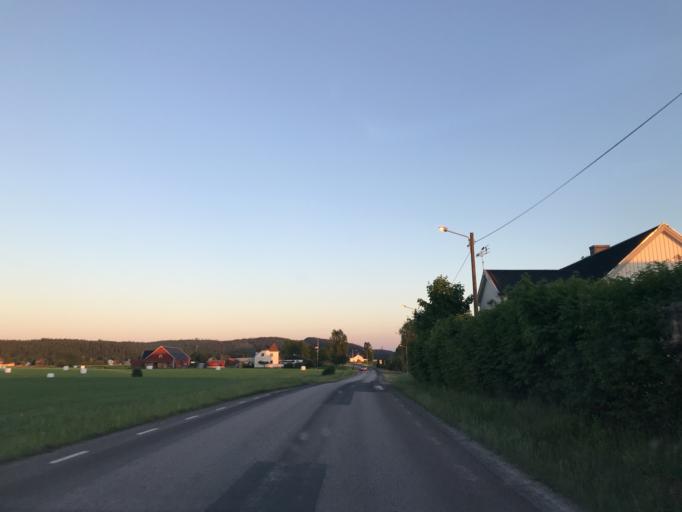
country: SE
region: Vaestra Goetaland
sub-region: Marks Kommun
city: Horred
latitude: 57.4357
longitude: 12.5162
